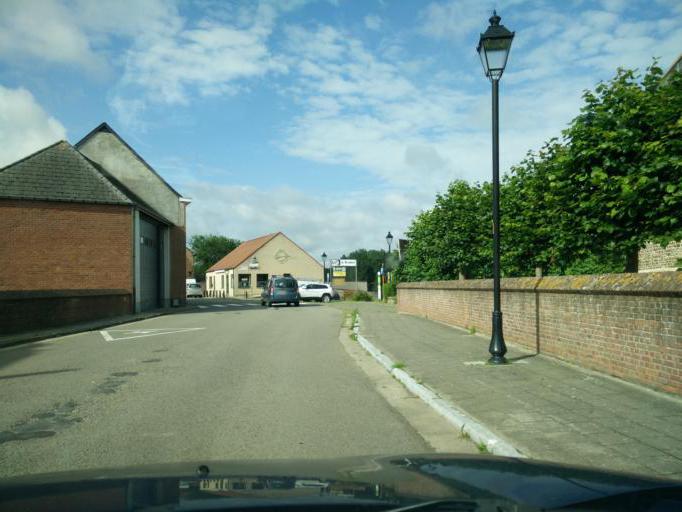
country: BE
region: Wallonia
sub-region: Province du Hainaut
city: Flobecq
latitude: 50.7928
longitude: 3.7482
